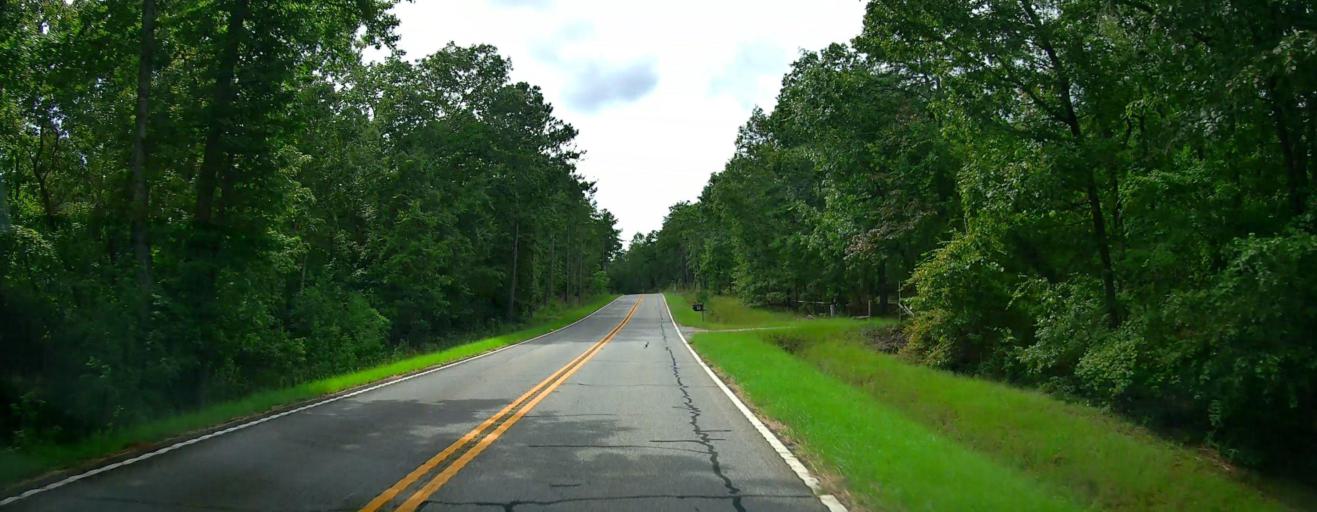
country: US
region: Georgia
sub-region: Meriwether County
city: Manchester
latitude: 32.8634
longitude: -84.7264
